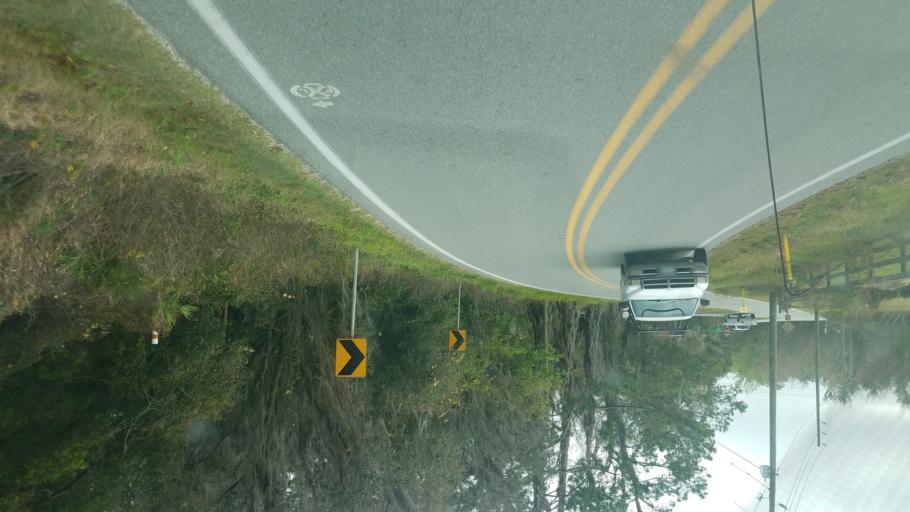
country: US
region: Florida
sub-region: Polk County
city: Kathleen
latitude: 28.1803
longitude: -82.0157
